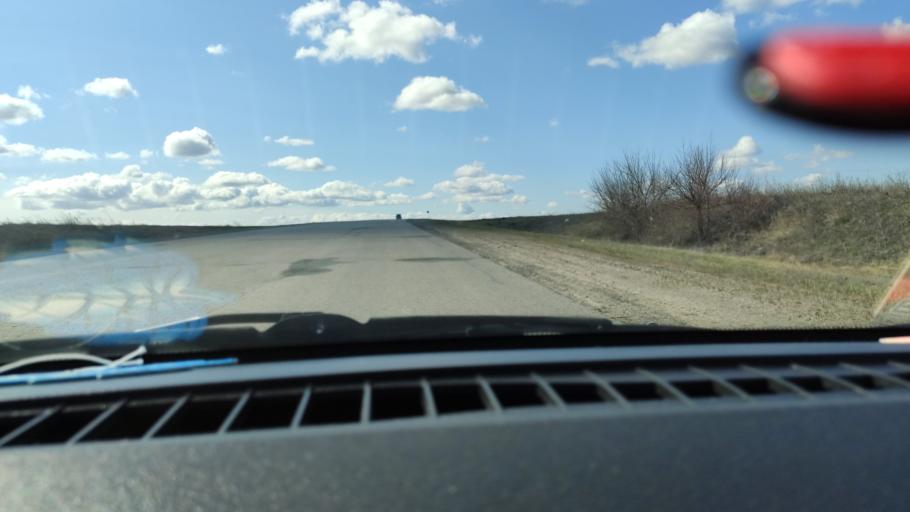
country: RU
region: Samara
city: Varlamovo
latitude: 53.0582
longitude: 48.3497
